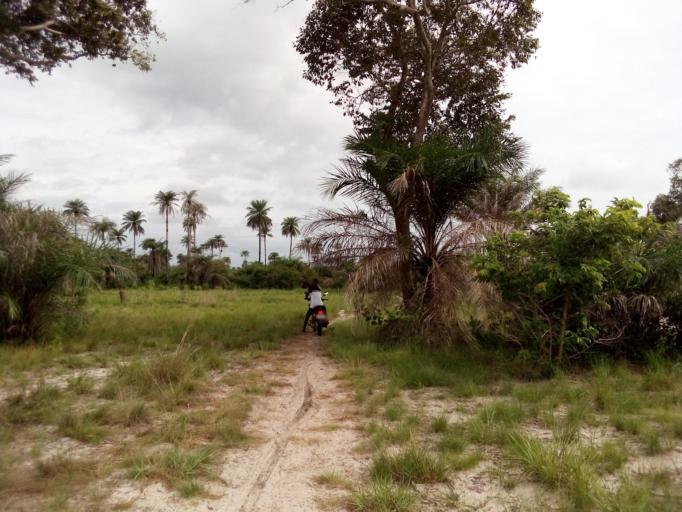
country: SL
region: Southern Province
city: Bonthe
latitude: 7.5169
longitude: -12.5701
